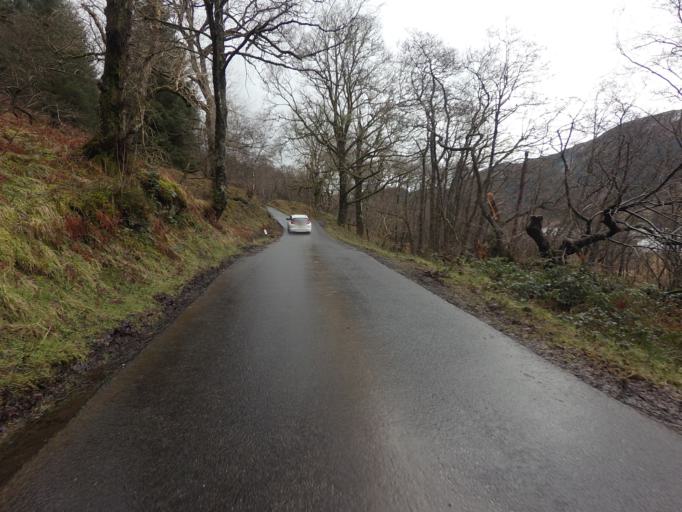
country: GB
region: Scotland
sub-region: West Dunbartonshire
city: Balloch
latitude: 56.2176
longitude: -4.5453
